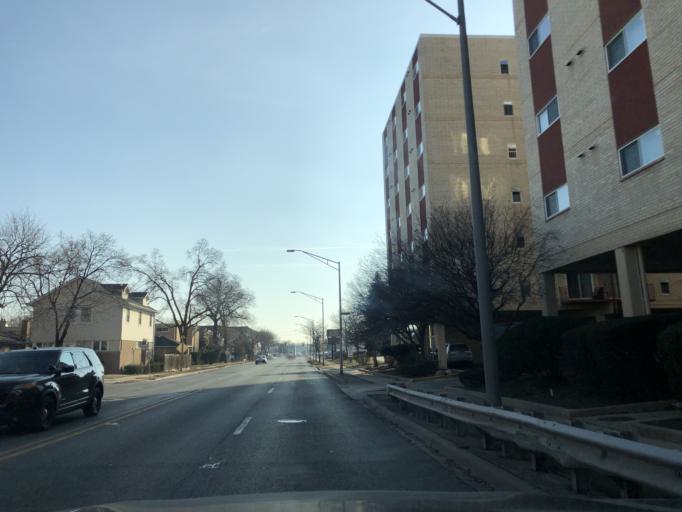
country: US
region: Illinois
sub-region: Cook County
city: Forest Park
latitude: 41.8676
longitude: -87.8190
